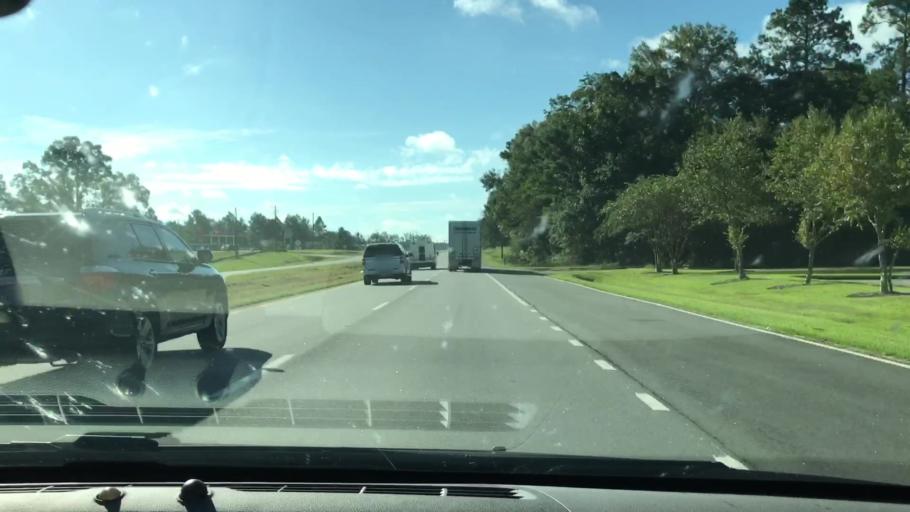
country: US
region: Georgia
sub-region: Dougherty County
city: Albany
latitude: 31.6396
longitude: -84.2511
